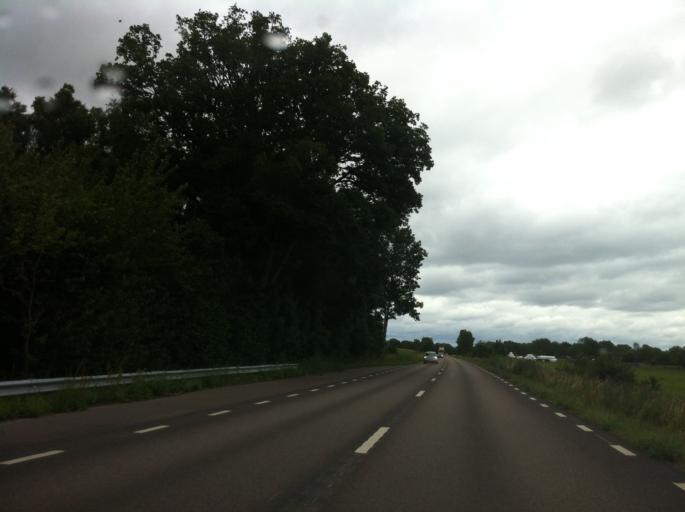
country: SE
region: Kalmar
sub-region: Borgholms Kommun
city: Borgholm
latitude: 57.1394
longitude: 16.9938
